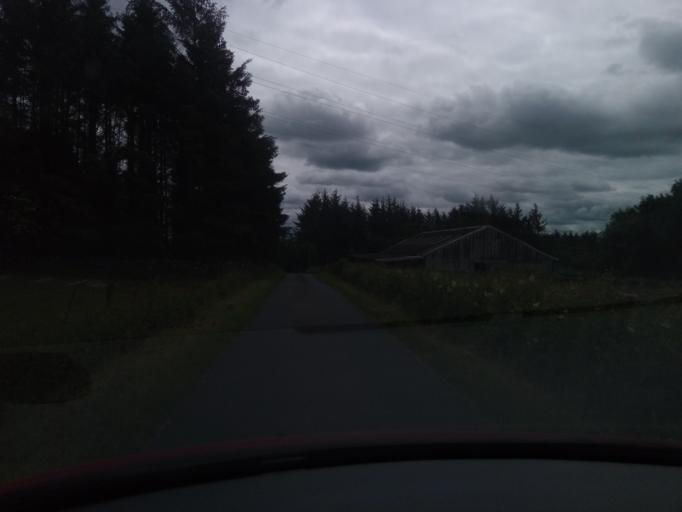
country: GB
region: Scotland
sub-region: The Scottish Borders
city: Hawick
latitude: 55.4333
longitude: -2.8237
